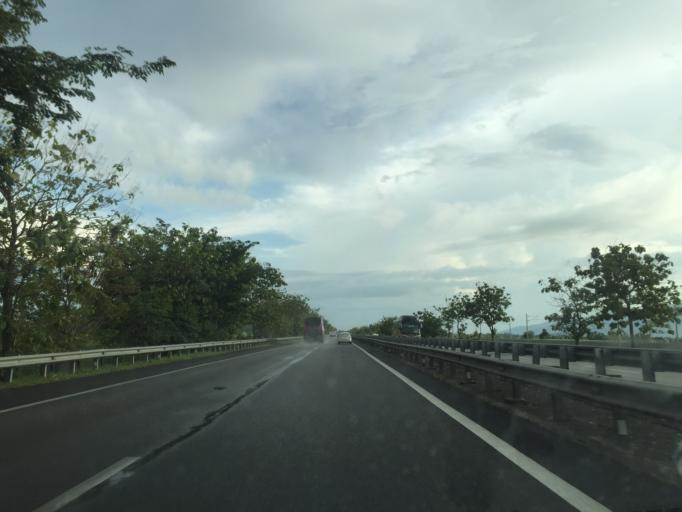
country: MY
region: Kedah
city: Gurun
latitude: 5.9248
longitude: 100.4649
